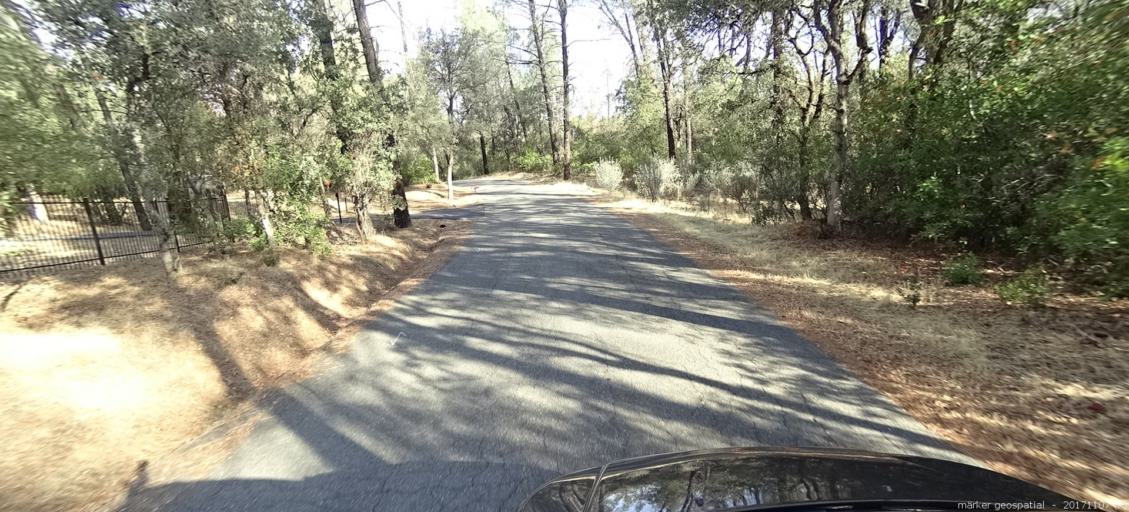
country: US
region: California
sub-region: Shasta County
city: Redding
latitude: 40.5501
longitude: -122.4469
